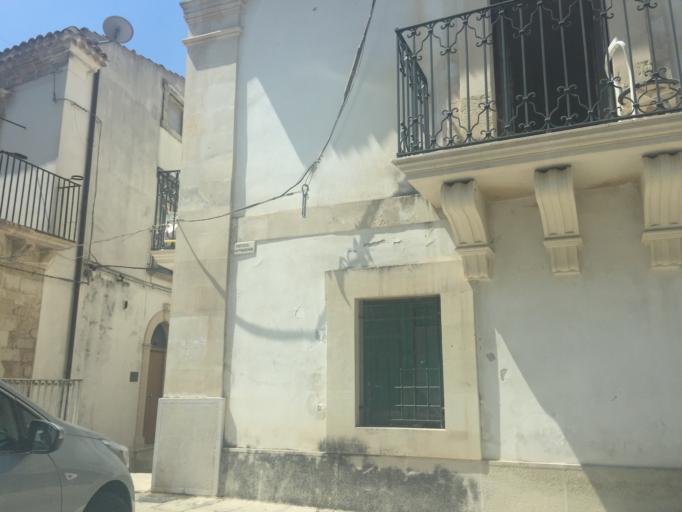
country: IT
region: Sicily
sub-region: Ragusa
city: Scicli
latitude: 36.7919
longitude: 14.7078
